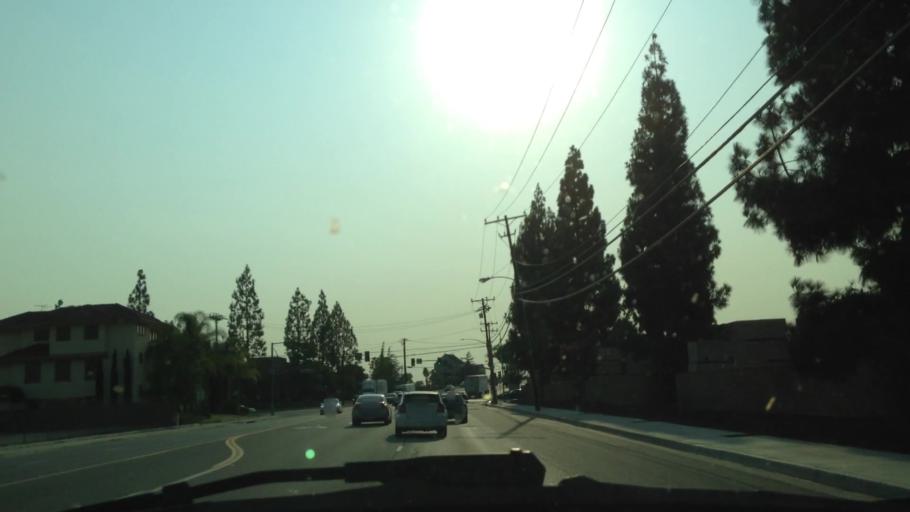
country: US
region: California
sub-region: Orange County
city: Orange
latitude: 33.8157
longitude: -117.8659
